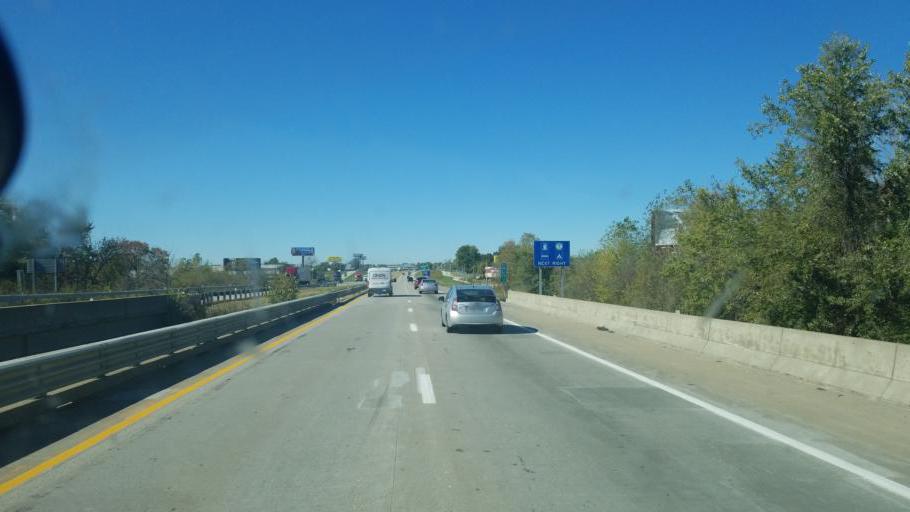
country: US
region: Missouri
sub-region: Jackson County
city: Grain Valley
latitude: 39.0206
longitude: -94.1832
